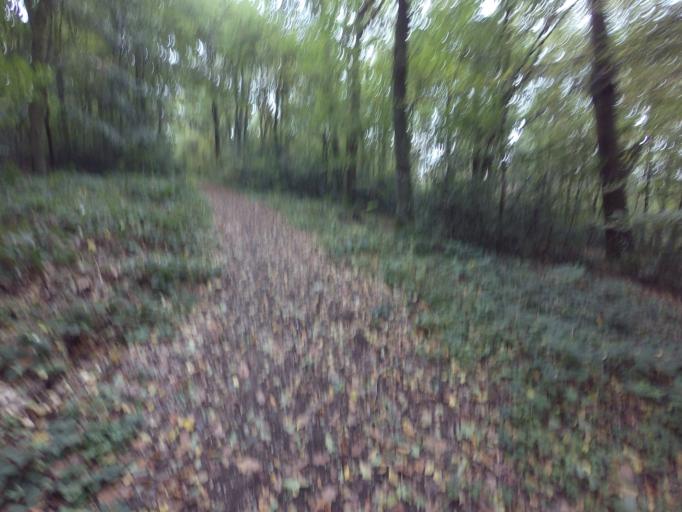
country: DE
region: North Rhine-Westphalia
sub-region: Regierungsbezirk Koln
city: Ubach-Palenberg
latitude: 50.9116
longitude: 6.0908
